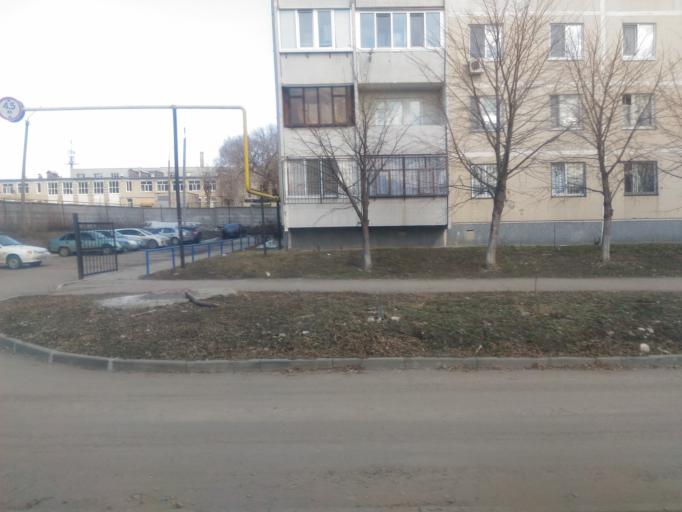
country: RU
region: Ulyanovsk
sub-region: Ulyanovskiy Rayon
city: Ulyanovsk
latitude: 54.3366
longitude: 48.3985
